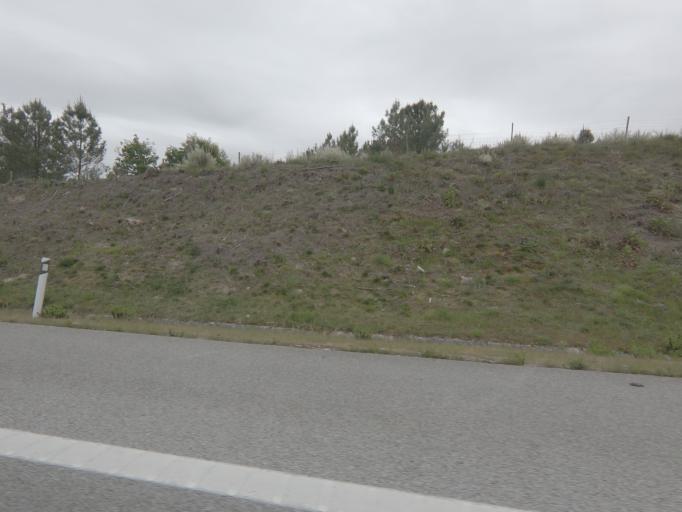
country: PT
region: Viseu
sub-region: Viseu
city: Viseu
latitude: 40.6241
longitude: -7.9399
